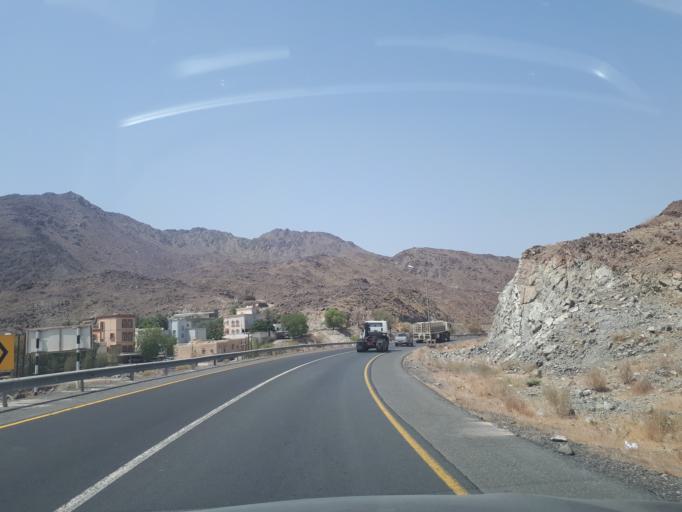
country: OM
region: Muhafazat ad Dakhiliyah
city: Sufalat Sama'il
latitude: 23.2528
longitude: 58.1012
